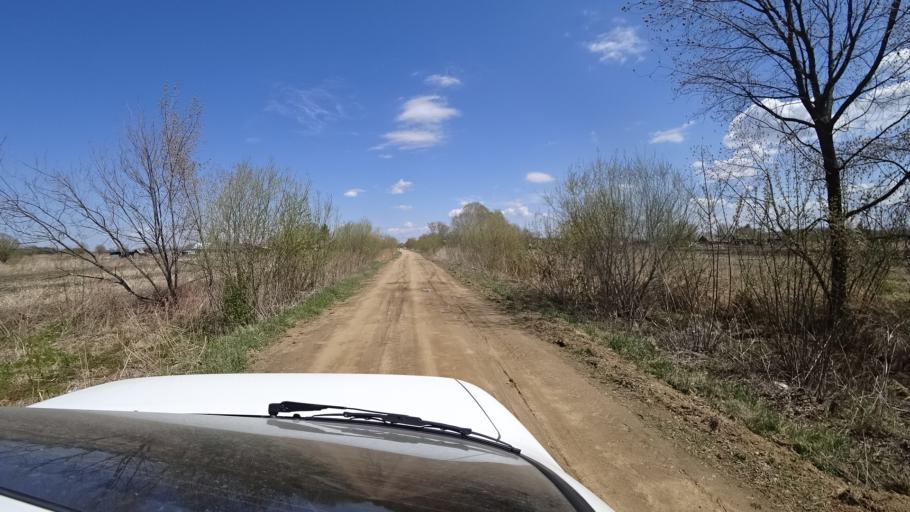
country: RU
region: Primorskiy
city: Dal'nerechensk
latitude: 45.7994
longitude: 133.7670
